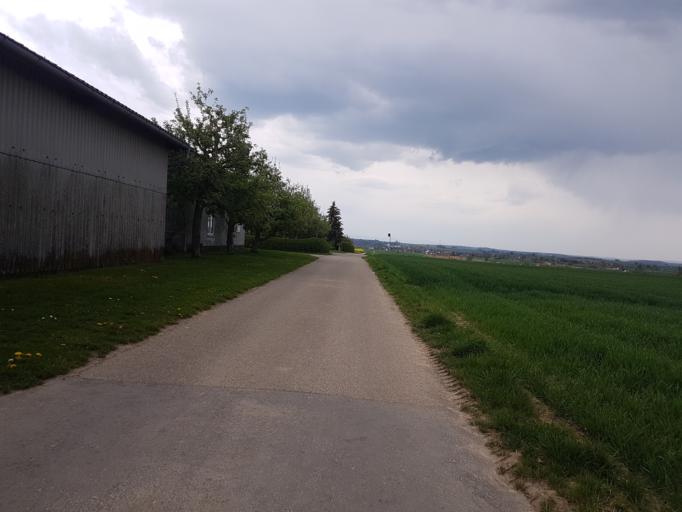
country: DE
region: Baden-Wuerttemberg
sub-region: Regierungsbezirk Stuttgart
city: Bondorf
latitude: 48.5133
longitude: 8.8086
